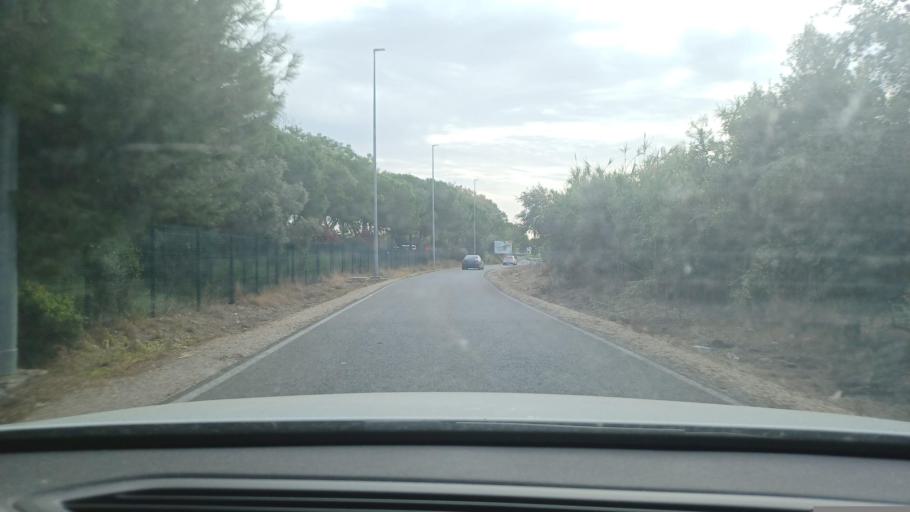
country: ES
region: Catalonia
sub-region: Provincia de Tarragona
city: Vila-seca
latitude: 41.0971
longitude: 1.1532
